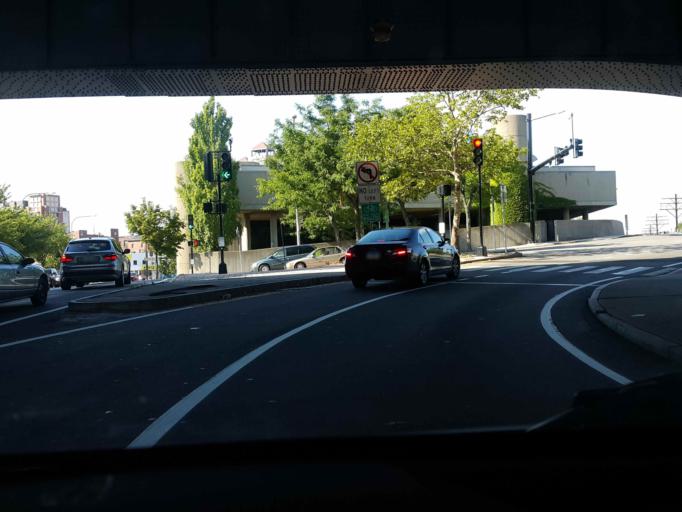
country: US
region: Connecticut
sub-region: New Haven County
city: New Haven
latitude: 41.3010
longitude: -72.9243
